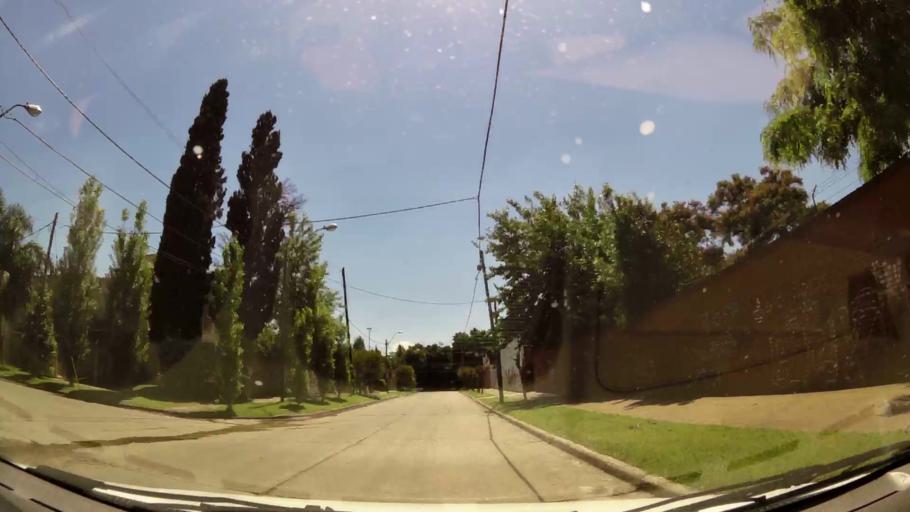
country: AR
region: Buenos Aires
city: Ituzaingo
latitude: -34.6620
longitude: -58.6847
